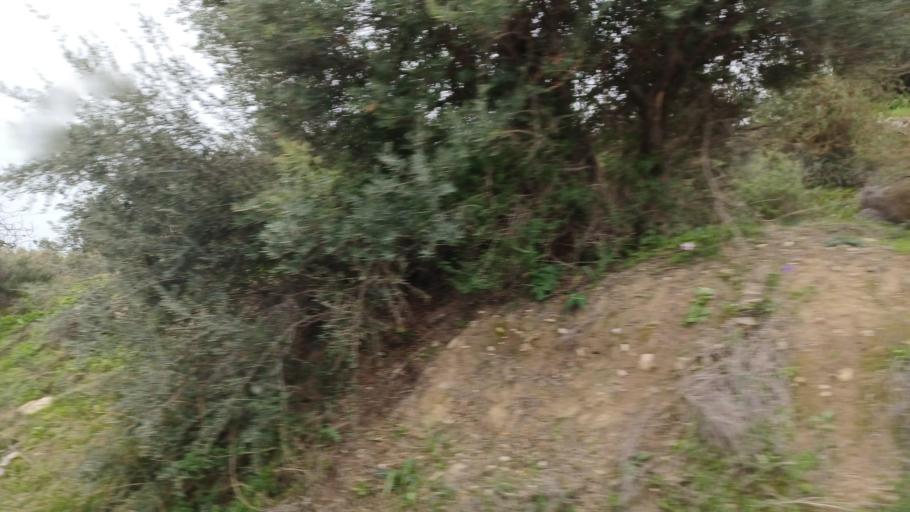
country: CY
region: Limassol
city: Pissouri
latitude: 34.6986
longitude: 32.7582
